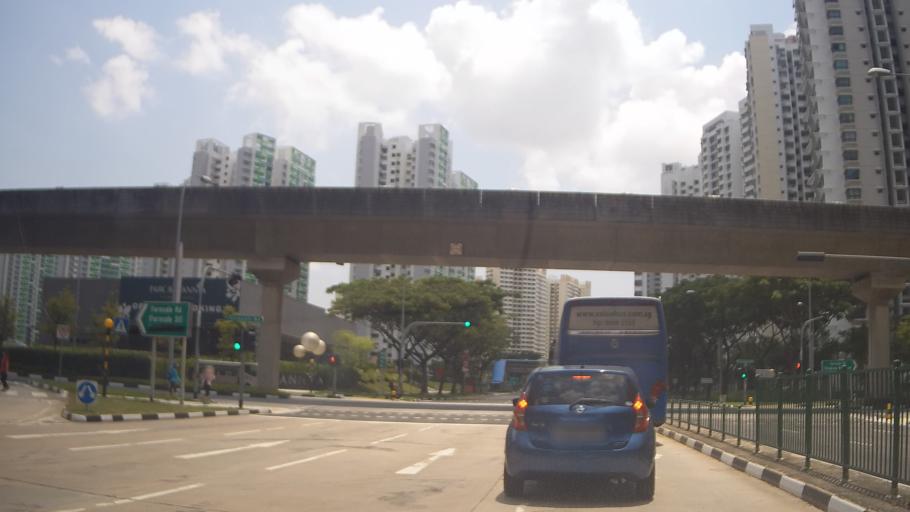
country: MY
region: Johor
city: Kampung Pasir Gudang Baru
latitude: 1.3950
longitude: 103.8752
